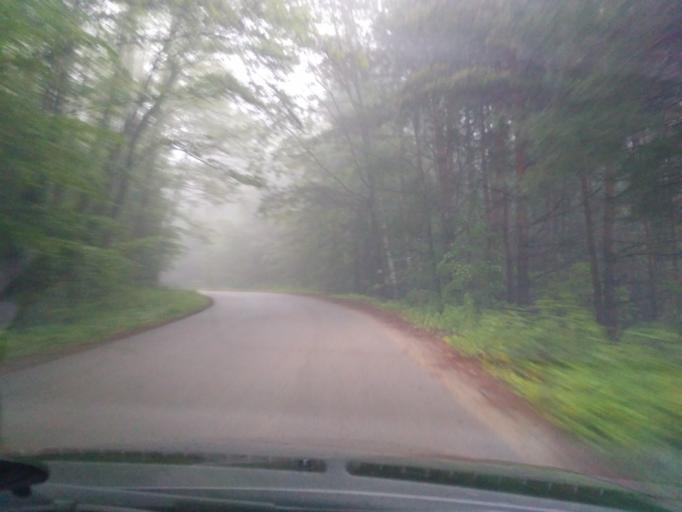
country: PL
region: Subcarpathian Voivodeship
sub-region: Powiat debicki
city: Debica
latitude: 49.9721
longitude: 21.3966
